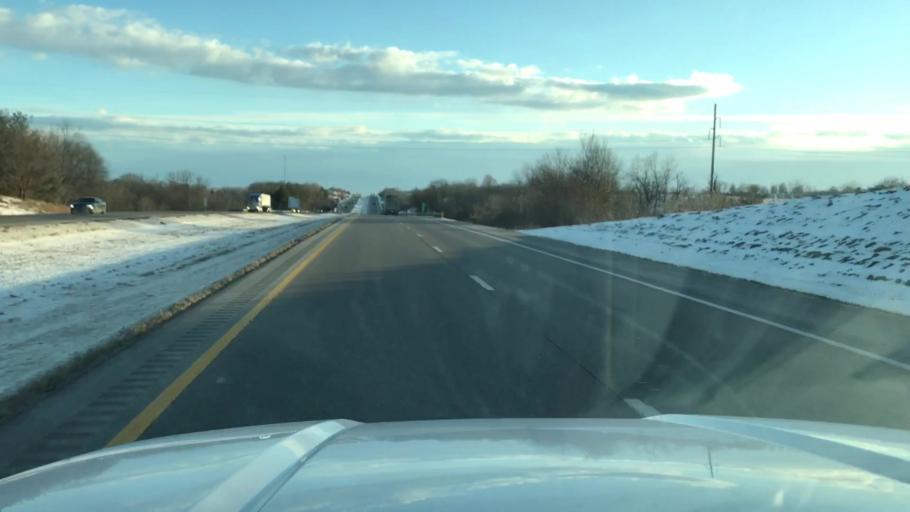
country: US
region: Missouri
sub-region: Andrew County
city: Country Club Village
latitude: 39.8445
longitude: -94.8057
